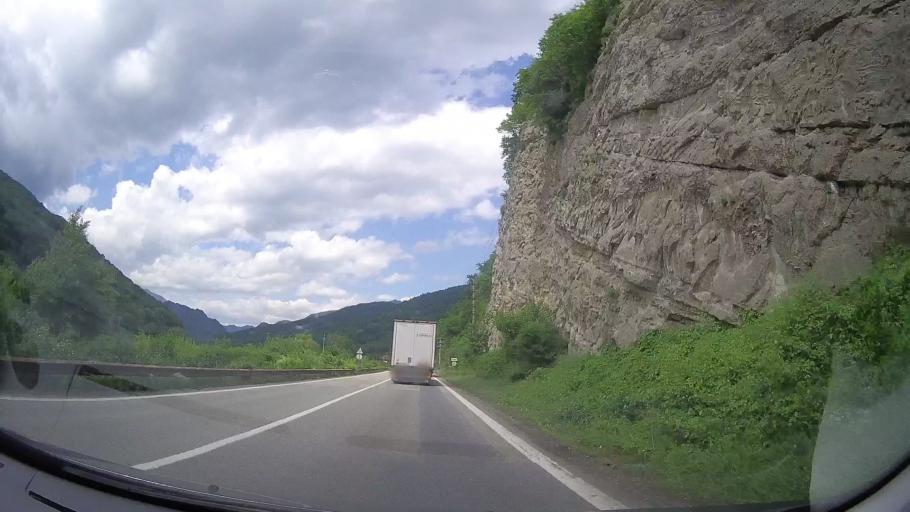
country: RO
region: Valcea
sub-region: Oras Calimanesti
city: Jiblea Veche
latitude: 45.2515
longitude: 24.3397
